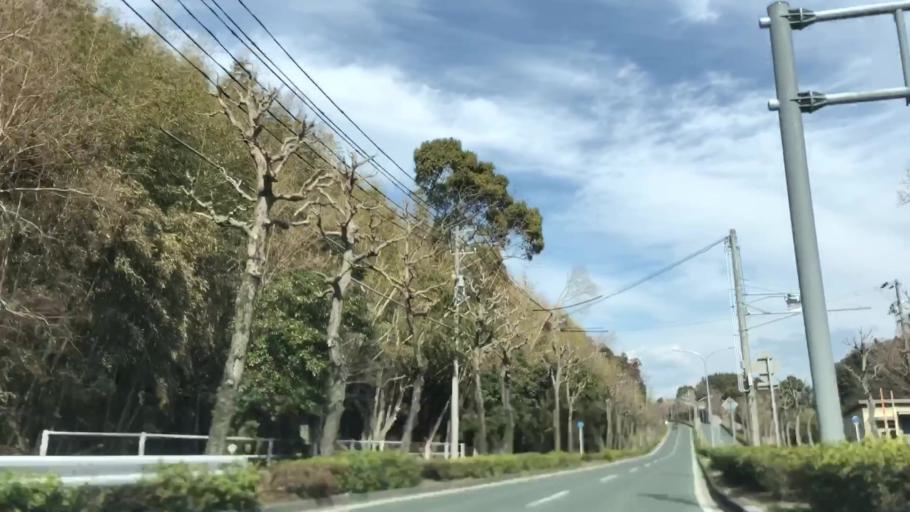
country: JP
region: Shizuoka
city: Hamamatsu
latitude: 34.7470
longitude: 137.6660
